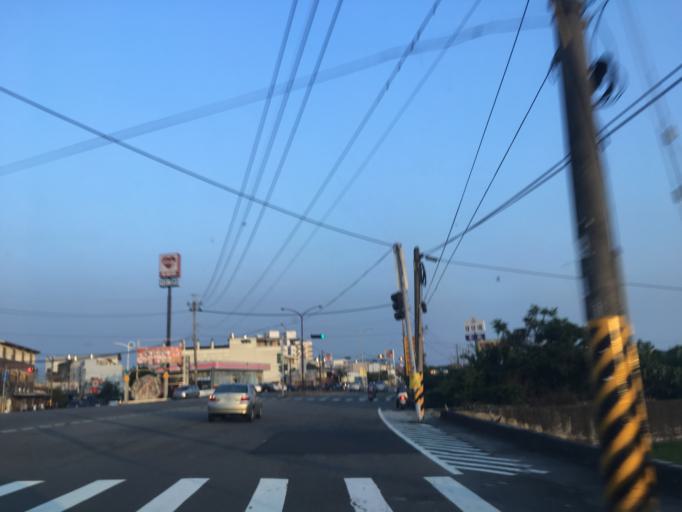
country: TW
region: Taiwan
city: Zhongxing New Village
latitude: 23.9956
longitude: 120.6649
